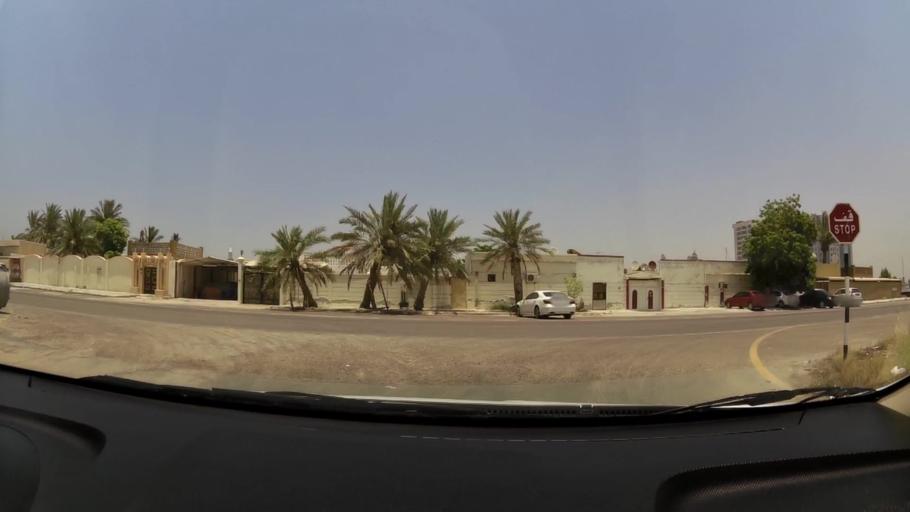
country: AE
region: Umm al Qaywayn
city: Umm al Qaywayn
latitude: 25.5494
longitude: 55.5429
